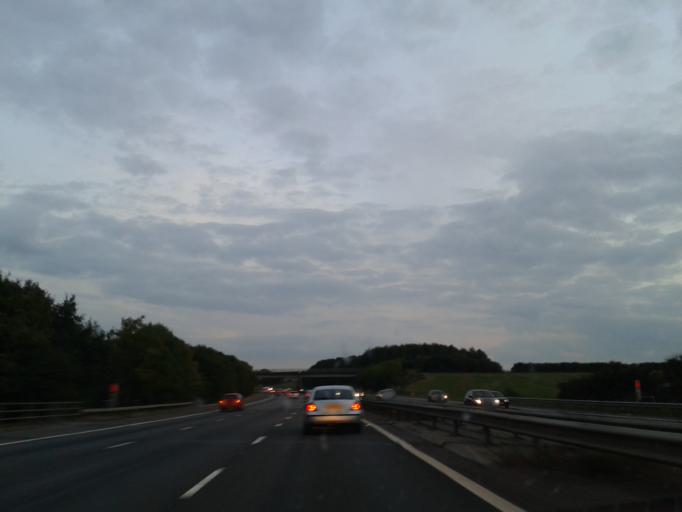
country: GB
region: England
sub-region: Oxfordshire
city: Somerton
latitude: 51.9822
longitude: -1.2650
